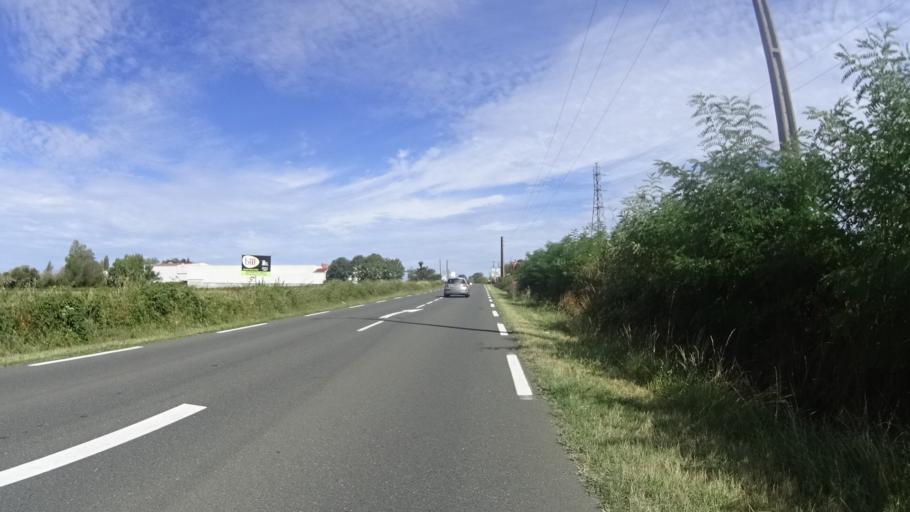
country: FR
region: Bourgogne
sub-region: Departement de Saone-et-Loire
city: Bourbon-Lancy
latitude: 46.6258
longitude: 3.7375
